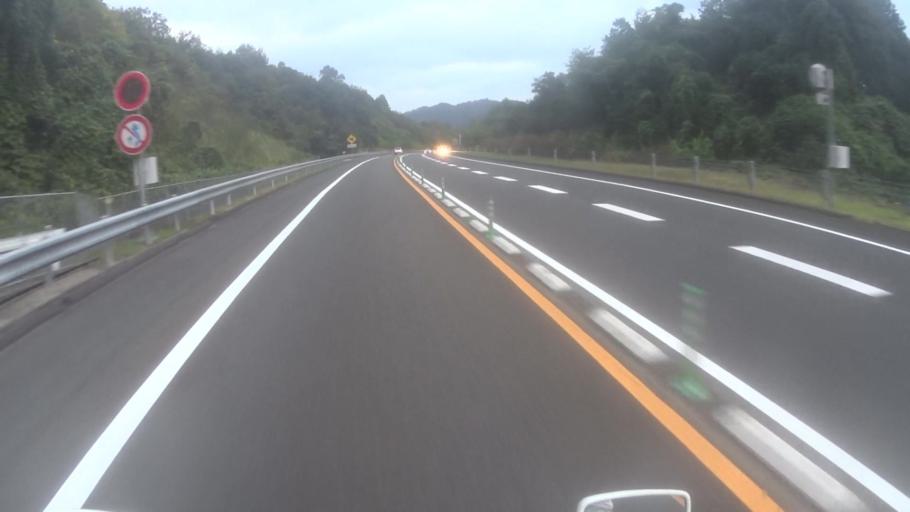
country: JP
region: Kyoto
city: Ayabe
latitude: 35.3932
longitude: 135.2383
